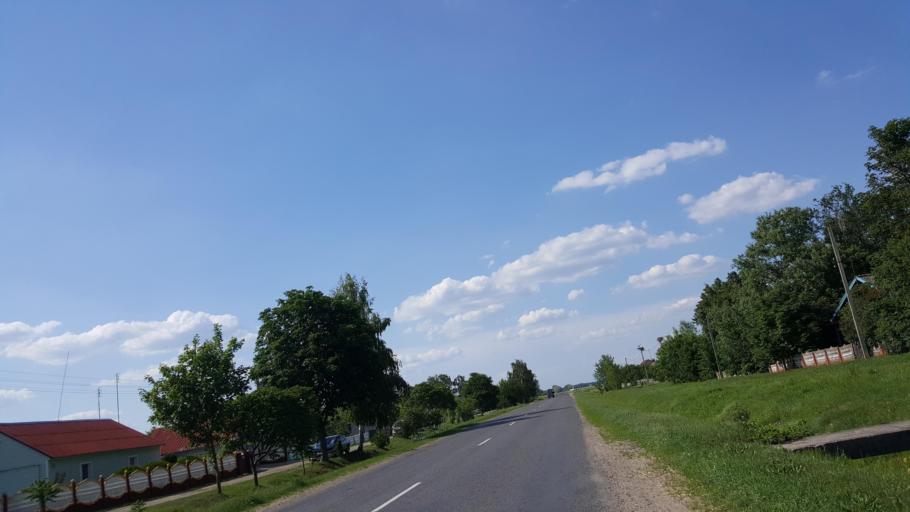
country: BY
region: Brest
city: Kobryn
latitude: 52.3065
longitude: 24.2732
